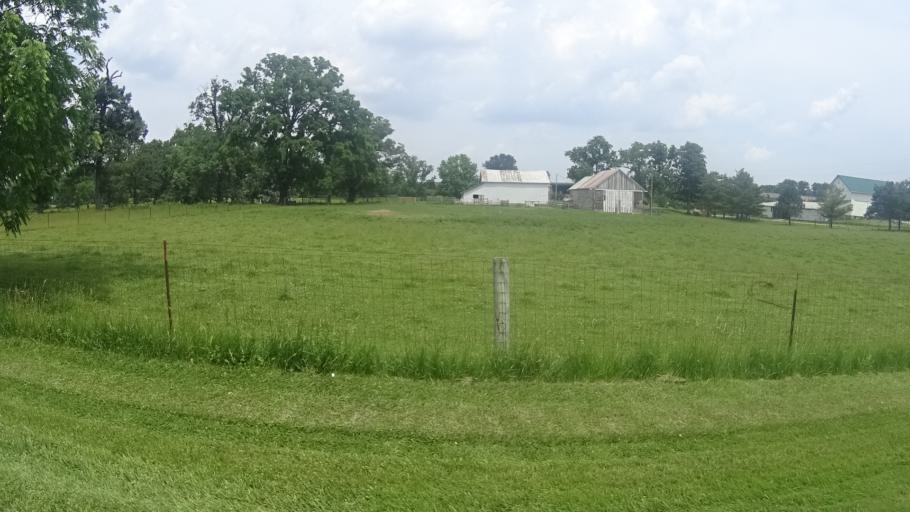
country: US
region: Ohio
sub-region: Erie County
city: Milan
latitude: 41.3226
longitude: -82.6323
